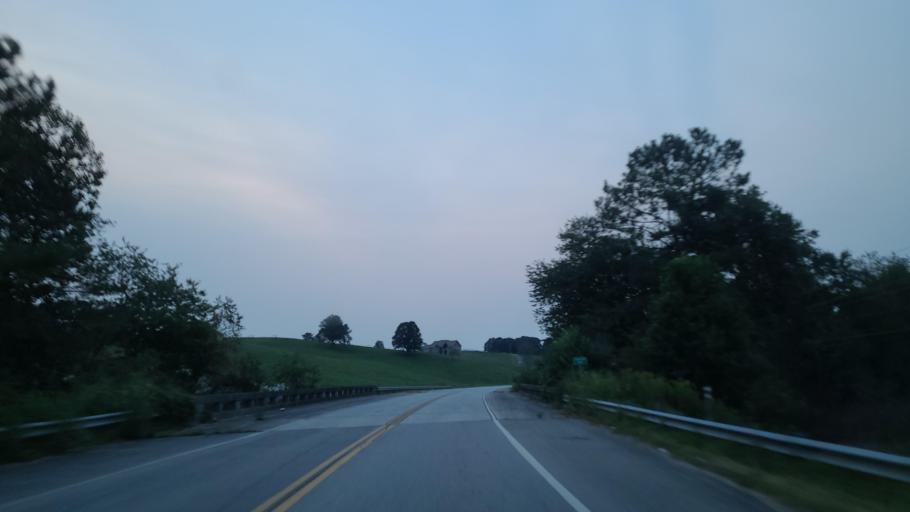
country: US
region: Georgia
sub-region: Union County
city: Blairsville
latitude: 34.8356
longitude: -84.0836
